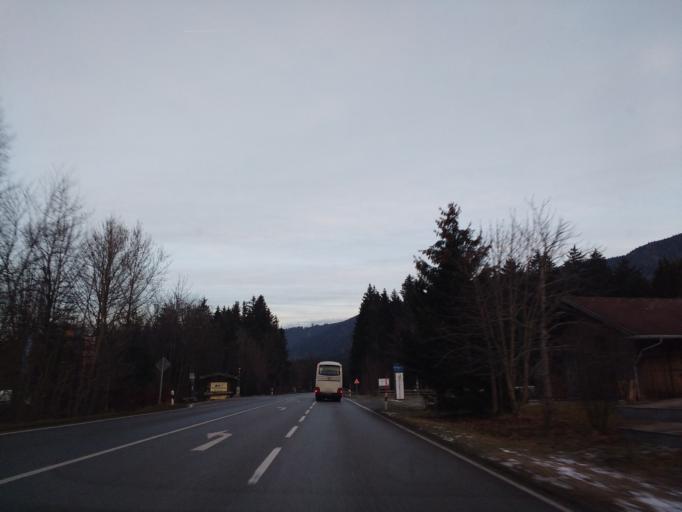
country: DE
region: Bavaria
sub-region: Swabia
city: Schwangau
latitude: 47.5914
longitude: 10.7722
